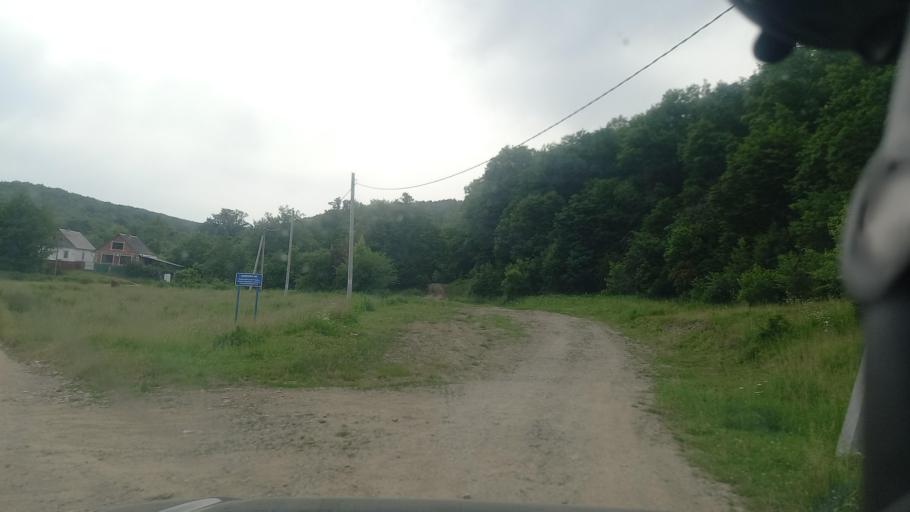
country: RU
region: Krasnodarskiy
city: Goryachiy Klyuch
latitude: 44.6056
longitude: 38.9913
